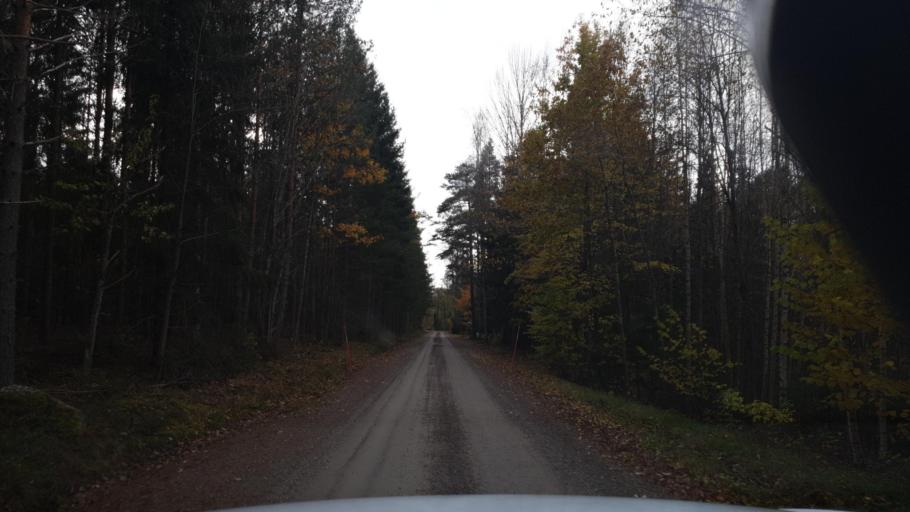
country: SE
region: Vaermland
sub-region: Arvika Kommun
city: Arvika
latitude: 59.5120
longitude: 12.7307
